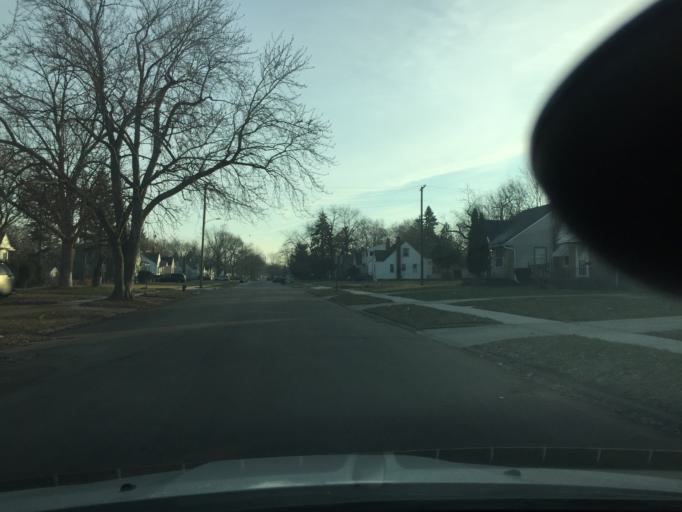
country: US
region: Michigan
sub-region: Macomb County
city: Eastpointe
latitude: 42.4382
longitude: -82.9590
